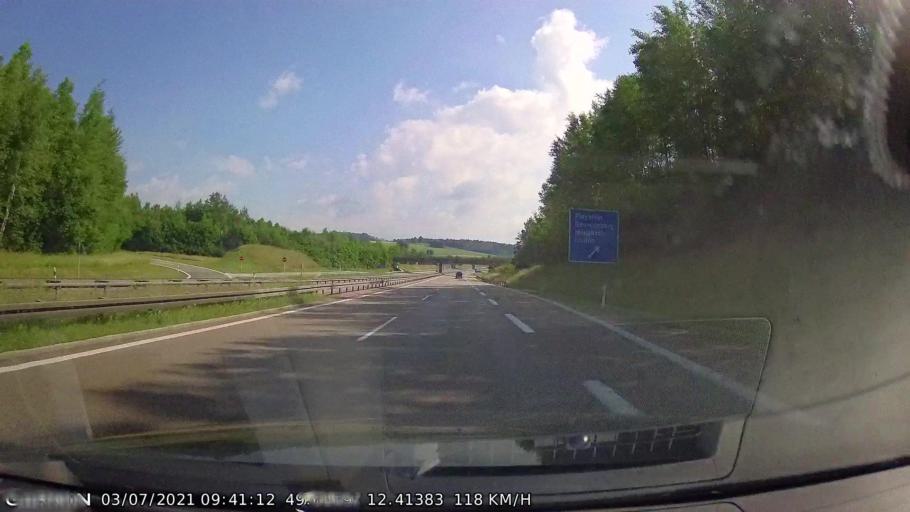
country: DE
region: Bavaria
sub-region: Upper Palatinate
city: Moosbach
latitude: 49.6171
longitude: 12.4140
